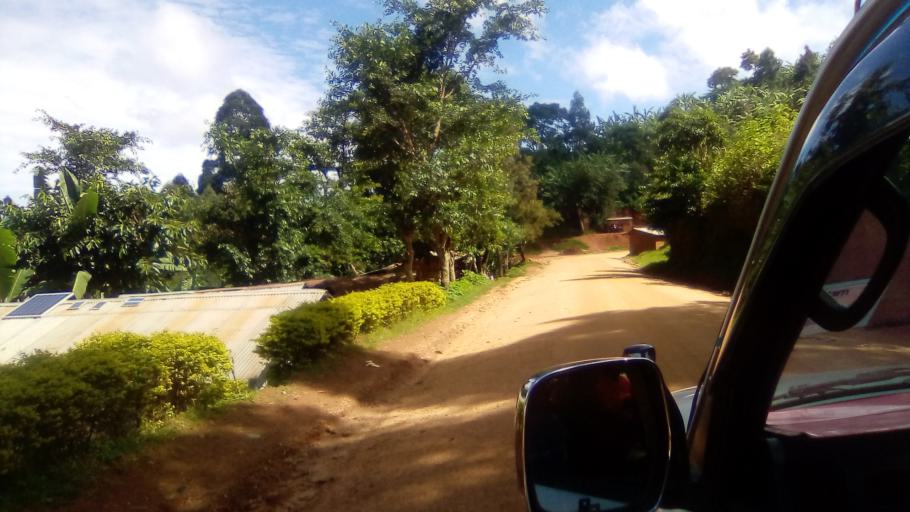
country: UG
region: Eastern Region
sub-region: Mbale District
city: Mbale
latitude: 1.0614
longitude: 34.2413
